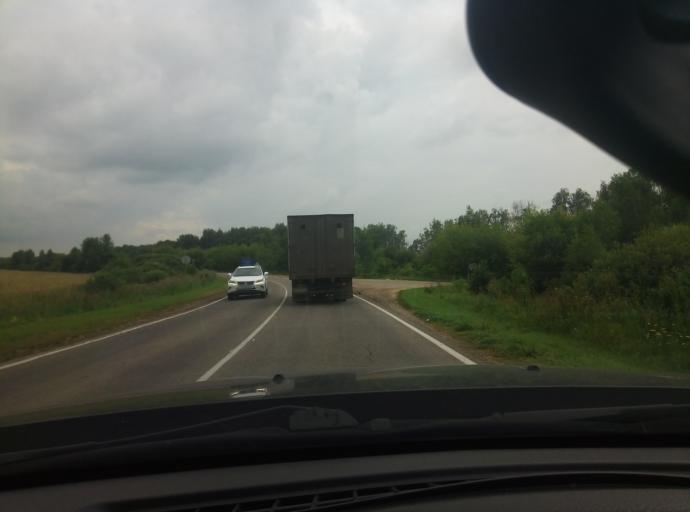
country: RU
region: Tula
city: Kimovsk
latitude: 53.9496
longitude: 38.5328
